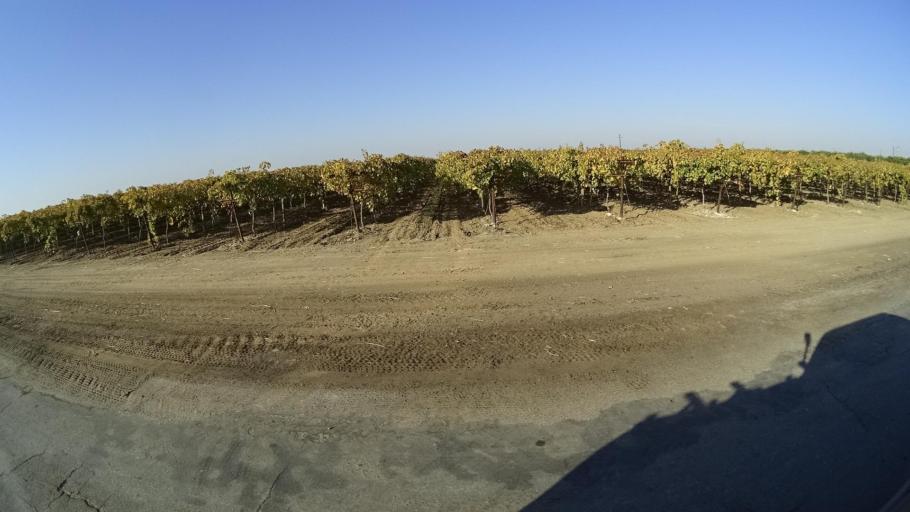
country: US
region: California
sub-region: Tulare County
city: Richgrove
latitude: 35.7715
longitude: -119.1607
